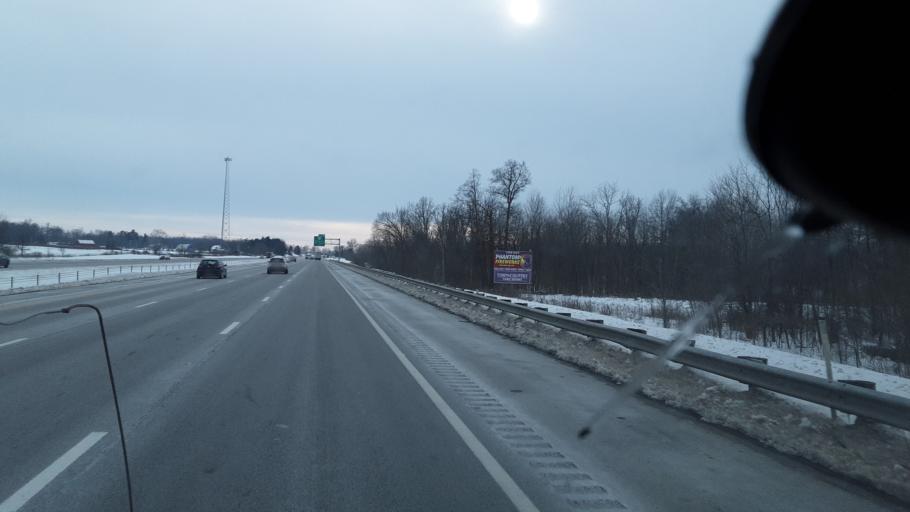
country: US
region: Ohio
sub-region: Wayne County
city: West Salem
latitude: 40.9607
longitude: -82.0632
